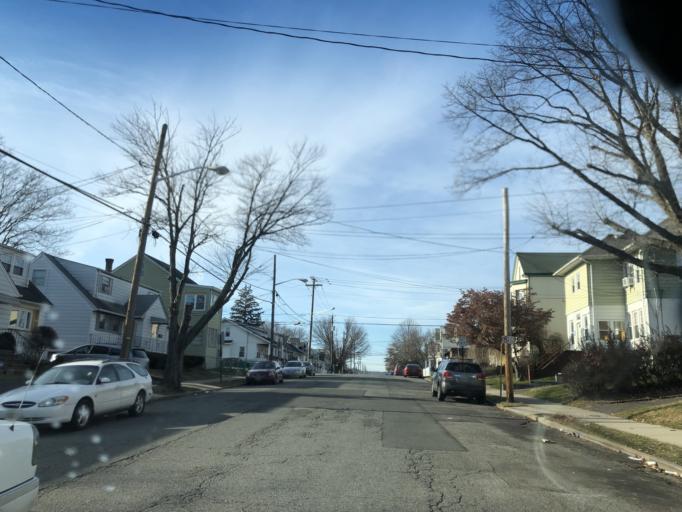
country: US
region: New Jersey
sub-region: Bergen County
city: Fair Lawn
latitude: 40.9263
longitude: -74.1465
